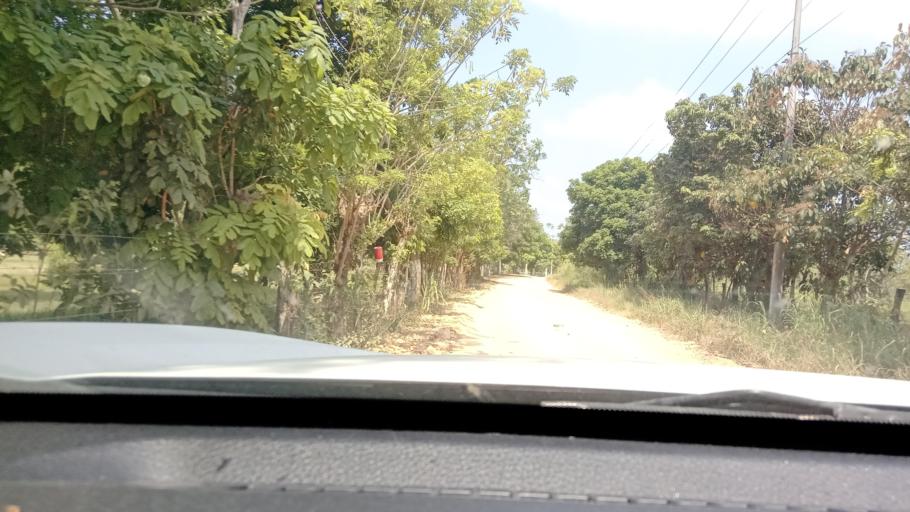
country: MX
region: Veracruz
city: Las Choapas
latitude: 17.9363
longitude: -94.1165
